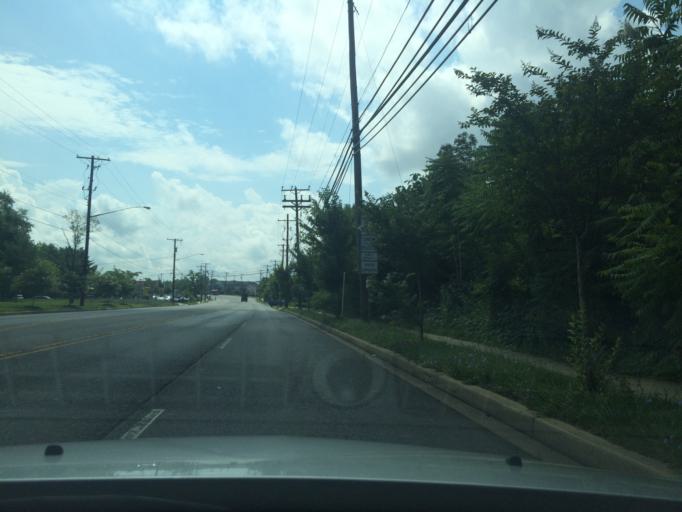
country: US
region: Maryland
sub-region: Prince George's County
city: District Heights
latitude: 38.8511
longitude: -76.8895
